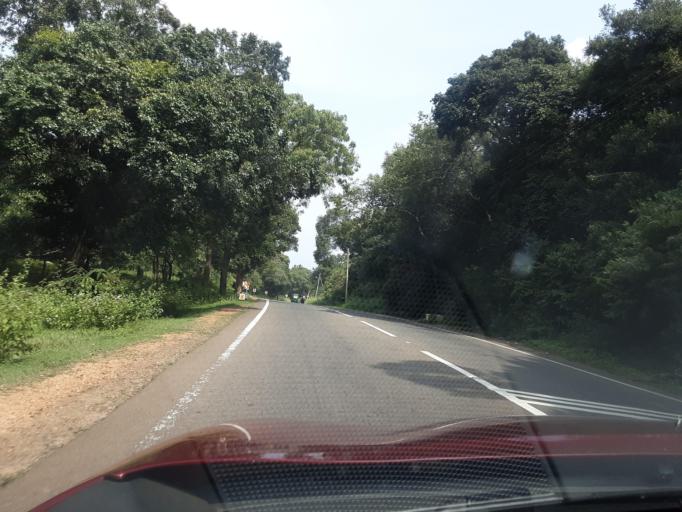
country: LK
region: North Central
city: Anuradhapura
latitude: 8.3488
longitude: 80.5081
